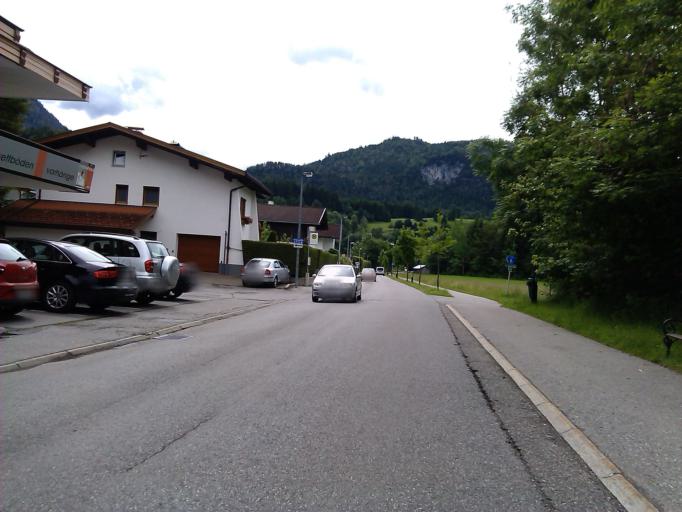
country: AT
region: Tyrol
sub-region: Politischer Bezirk Reutte
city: Reutte
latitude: 47.4792
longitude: 10.7214
